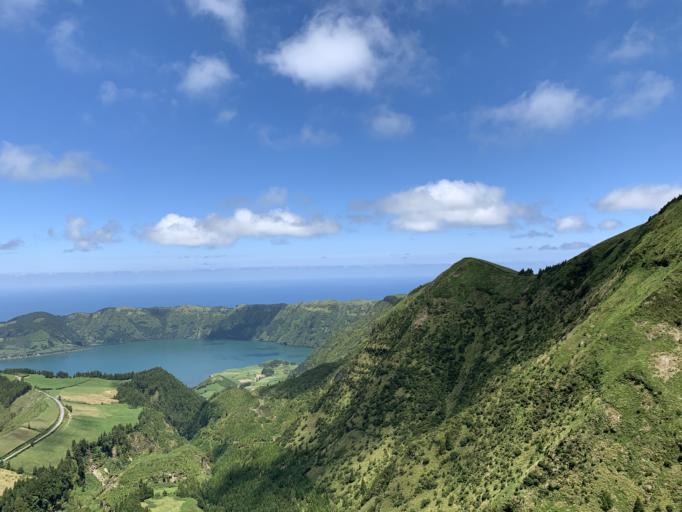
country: PT
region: Azores
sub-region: Ponta Delgada
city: Arrifes
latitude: 37.8424
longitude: -25.7609
